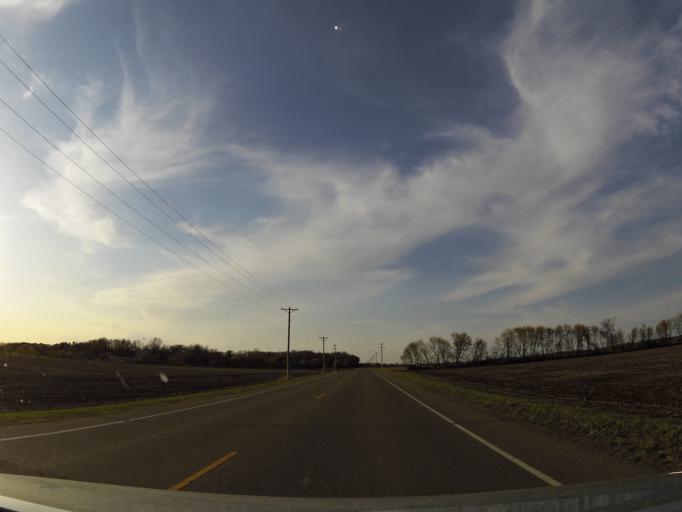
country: US
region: Wisconsin
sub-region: Pierce County
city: River Falls
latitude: 44.9006
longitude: -92.6742
